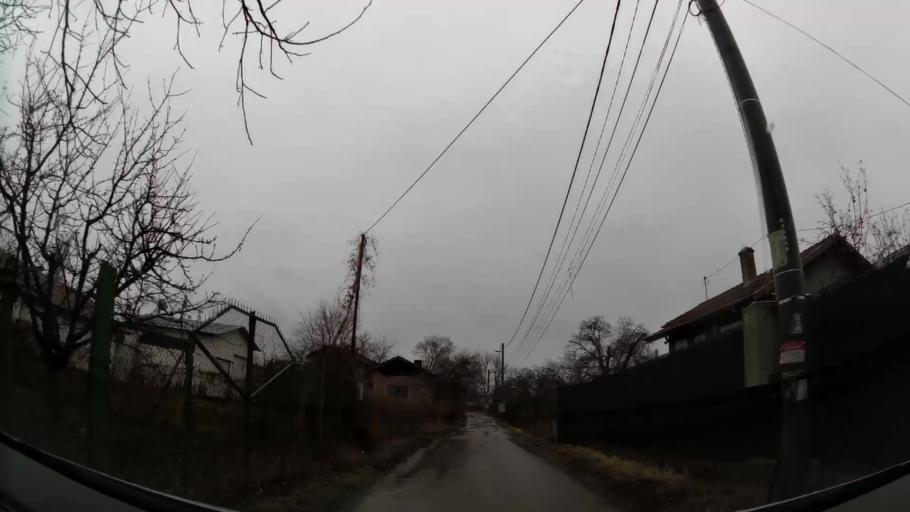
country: BG
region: Sofia-Capital
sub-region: Stolichna Obshtina
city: Sofia
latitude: 42.6553
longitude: 23.4287
